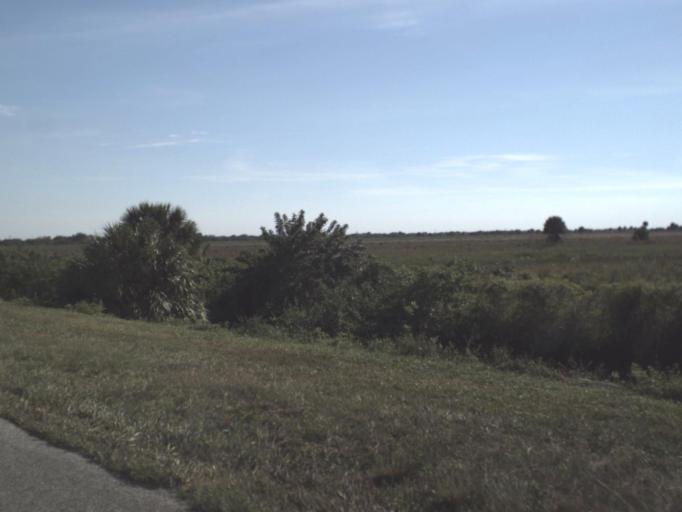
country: US
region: Florida
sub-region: Glades County
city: Moore Haven
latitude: 26.8367
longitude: -81.1930
